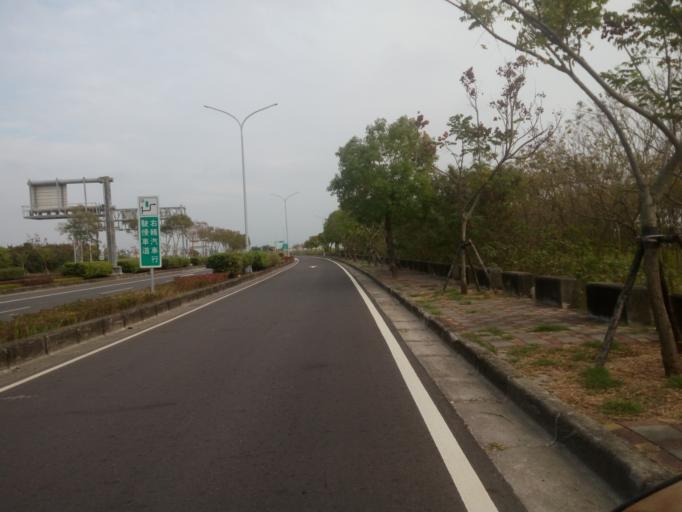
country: TW
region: Taiwan
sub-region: Chiayi
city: Taibao
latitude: 23.4829
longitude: 120.3698
